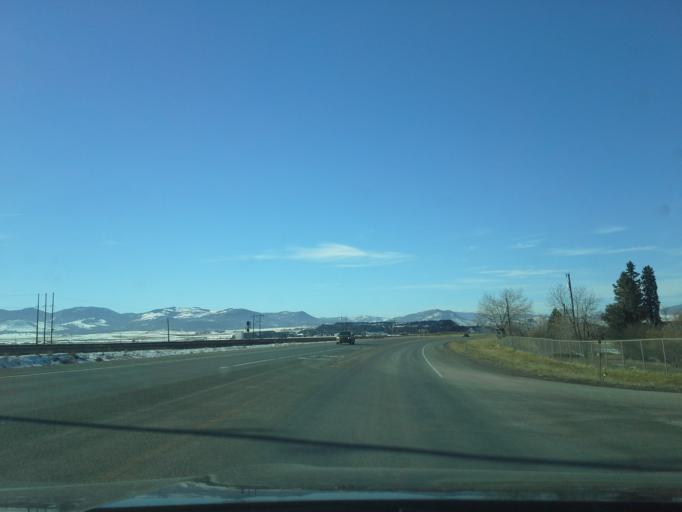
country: US
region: Montana
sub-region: Lewis and Clark County
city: East Helena
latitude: 46.5856
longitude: -111.8989
